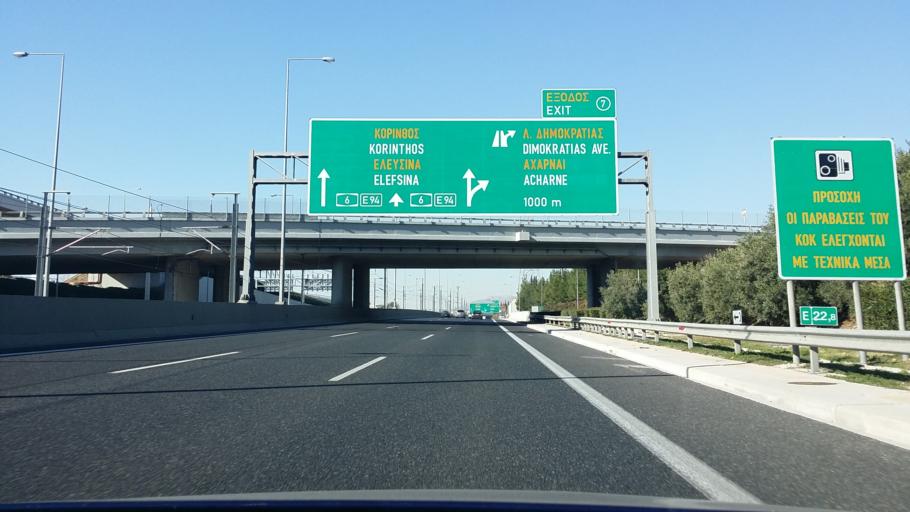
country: GR
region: Attica
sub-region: Nomarchia Athinas
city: Metamorfosi
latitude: 38.0629
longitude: 23.7472
